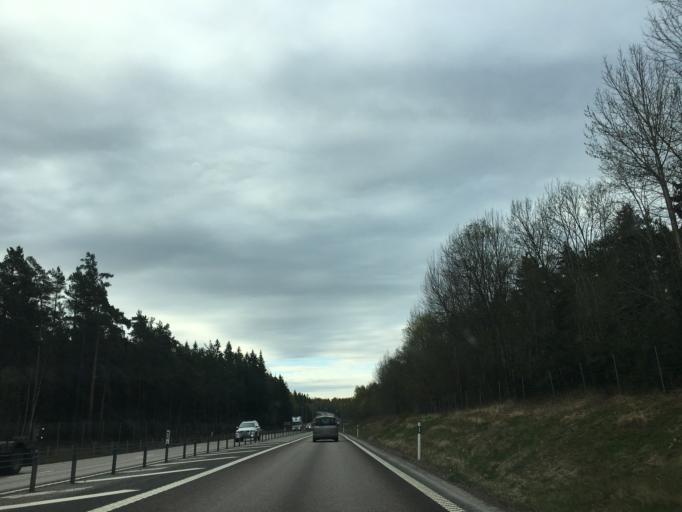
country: SE
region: Vaermland
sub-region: Kristinehamns Kommun
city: Kristinehamn
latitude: 59.3350
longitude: 14.0938
